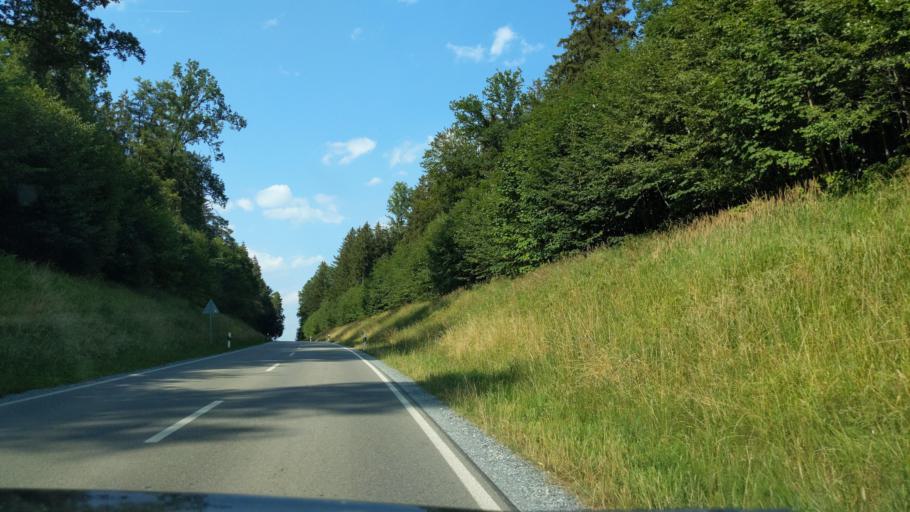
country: DE
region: Bavaria
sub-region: Upper Bavaria
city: Glonn
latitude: 47.9927
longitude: 11.8855
